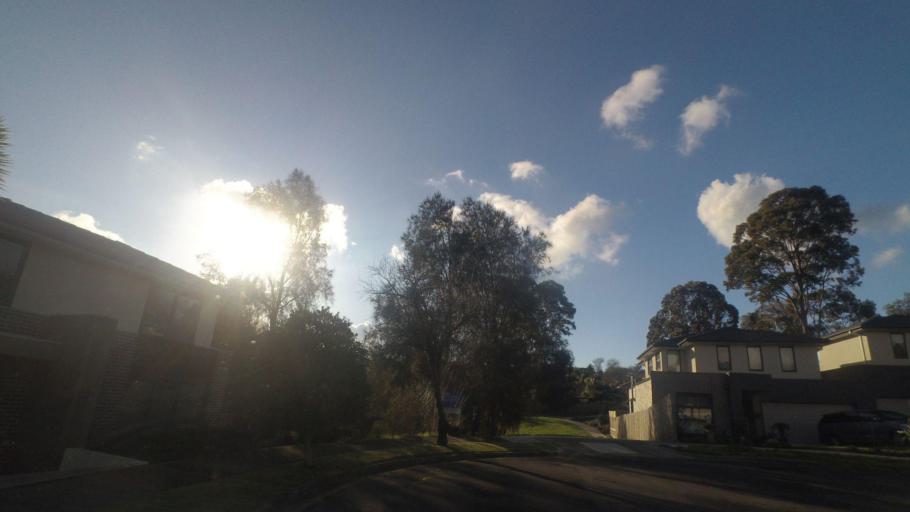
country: AU
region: Victoria
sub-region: Manningham
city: Templestowe Lower
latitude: -37.7764
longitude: 145.1101
